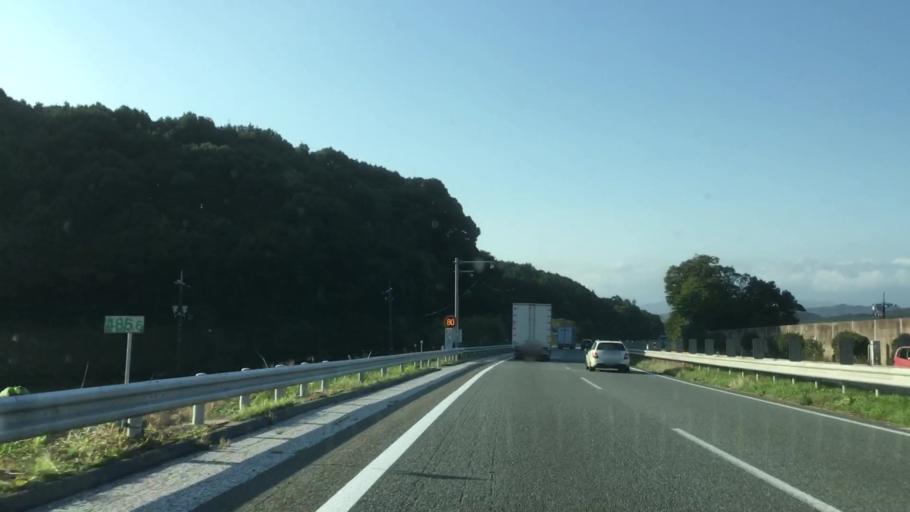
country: JP
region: Yamaguchi
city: Ogori-shimogo
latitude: 34.1465
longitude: 131.3451
